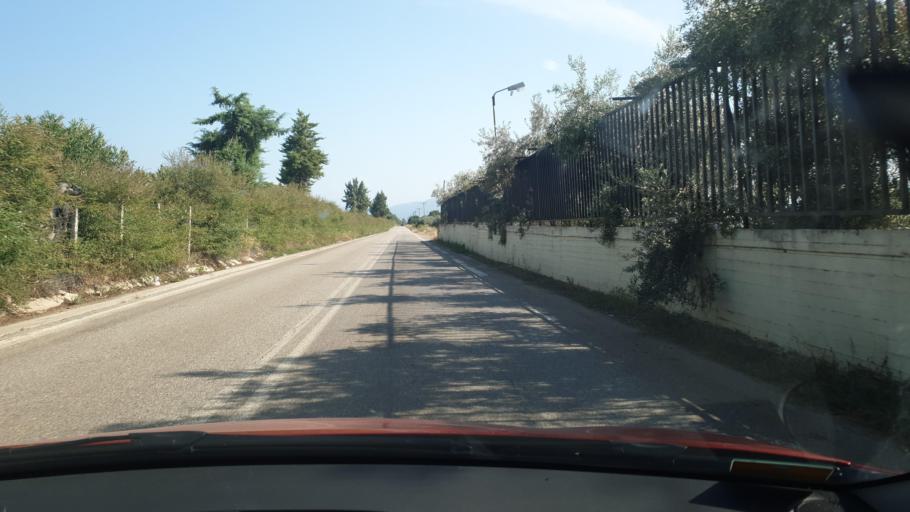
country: GR
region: Central Greece
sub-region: Nomos Fthiotidos
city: Livanates
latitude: 38.7214
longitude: 23.0520
